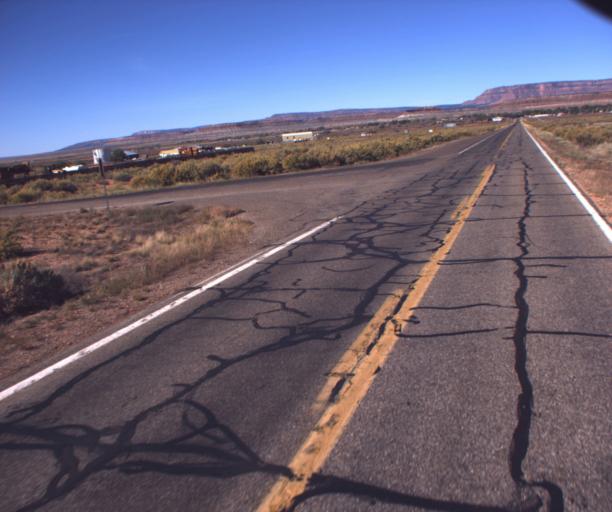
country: US
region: Arizona
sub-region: Coconino County
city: Fredonia
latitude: 36.9341
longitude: -112.5039
